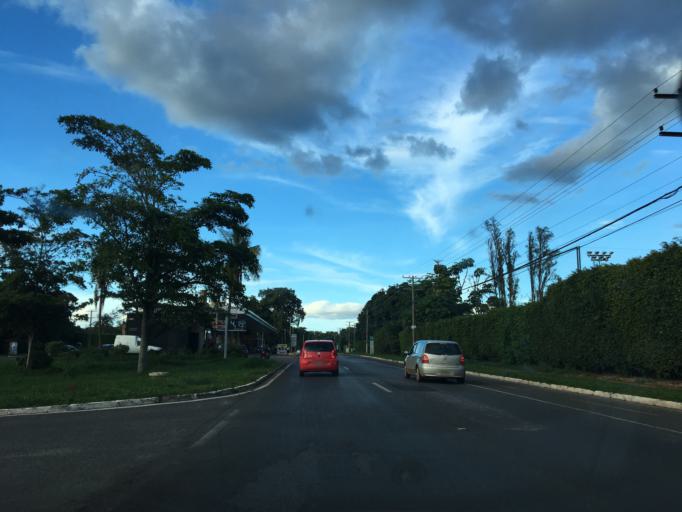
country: BR
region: Federal District
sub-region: Brasilia
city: Brasilia
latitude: -15.8502
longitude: -47.8560
